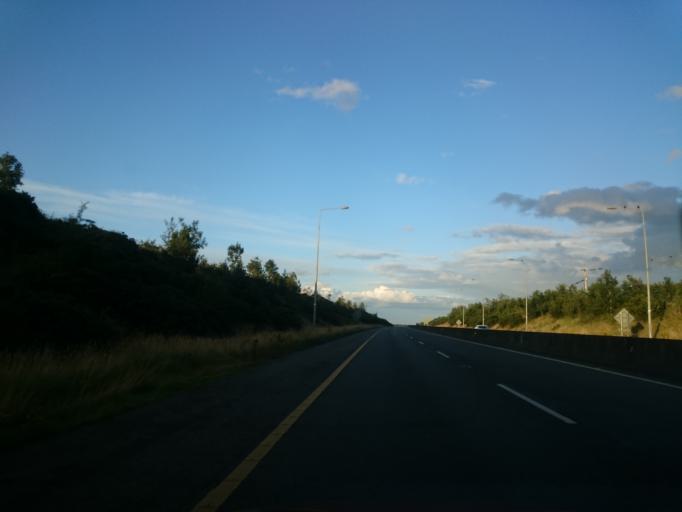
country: IE
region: Leinster
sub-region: Loch Garman
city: Gorey
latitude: 52.6333
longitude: -6.3715
